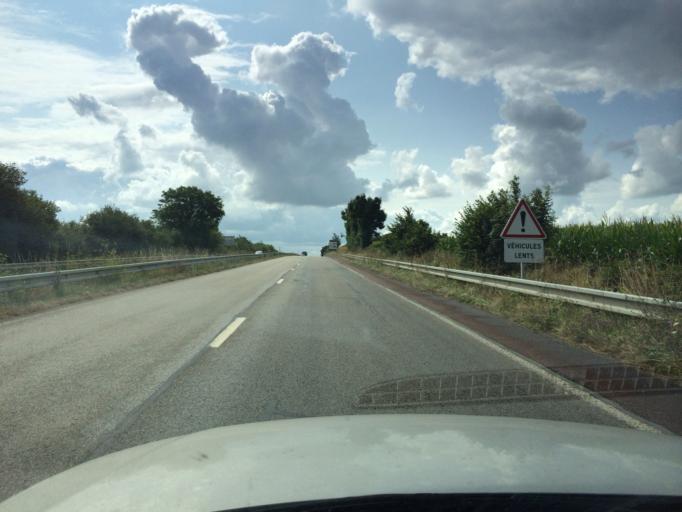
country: FR
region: Lower Normandy
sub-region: Departement de la Manche
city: Montebourg
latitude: 49.4573
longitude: -1.3553
